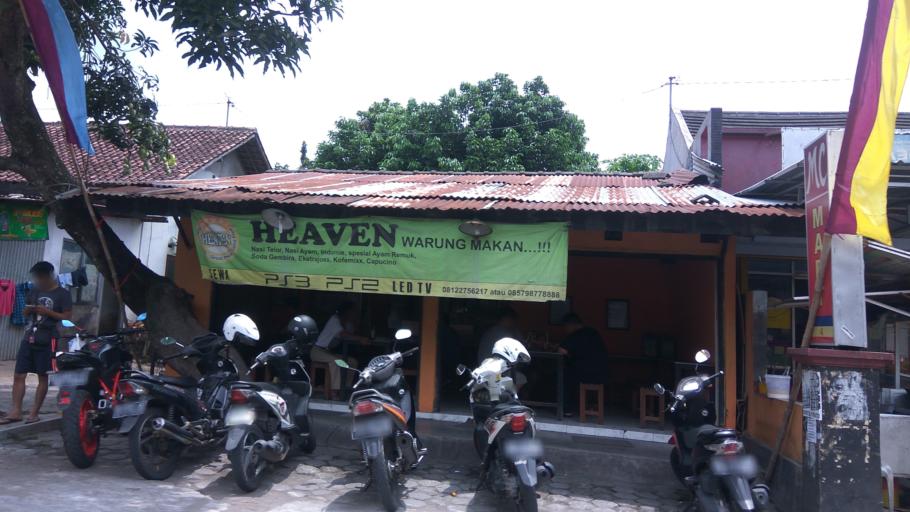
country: ID
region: Daerah Istimewa Yogyakarta
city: Depok
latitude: -7.7493
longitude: 110.4062
